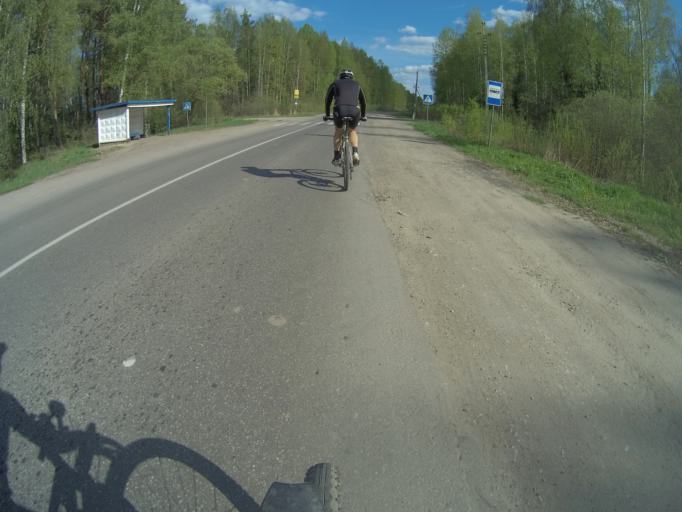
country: RU
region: Vladimir
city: Raduzhnyy
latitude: 55.9961
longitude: 40.2057
